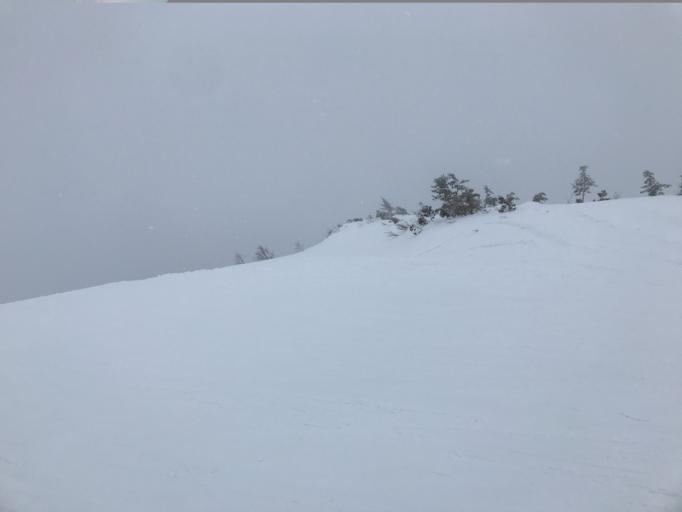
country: JP
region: Nagano
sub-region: Kitaazumi Gun
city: Hakuba
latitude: 36.7026
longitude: 137.8122
